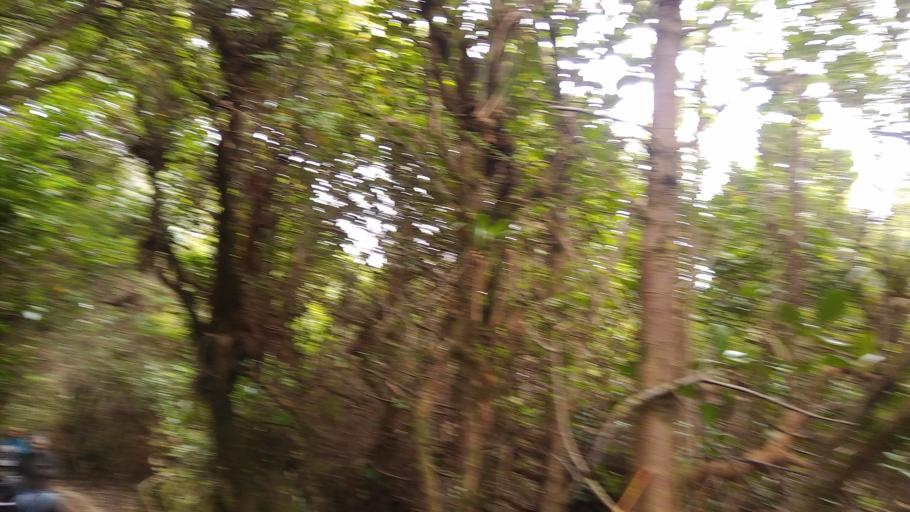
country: CR
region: Alajuela
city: Rio Segundo
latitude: 10.1902
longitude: -84.2298
